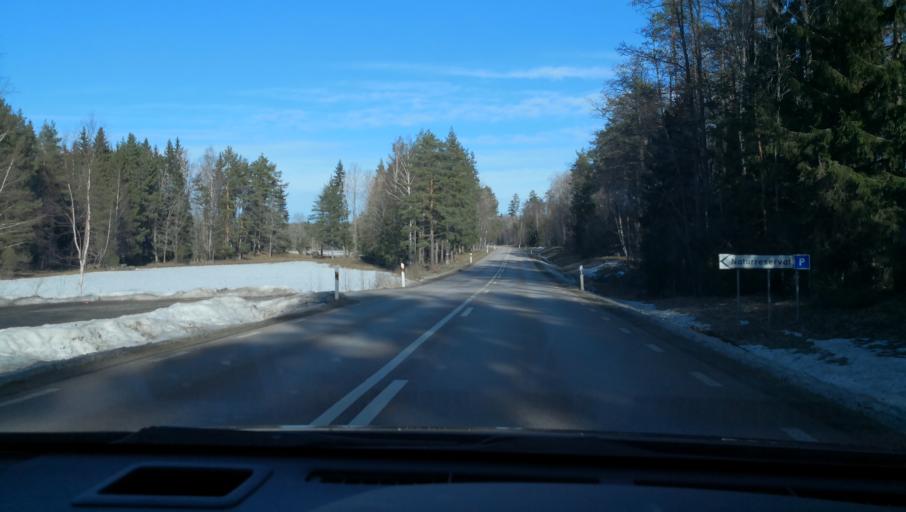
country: SE
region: Uppsala
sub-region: Osthammars Kommun
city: Osterbybruk
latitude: 60.1527
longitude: 17.8320
